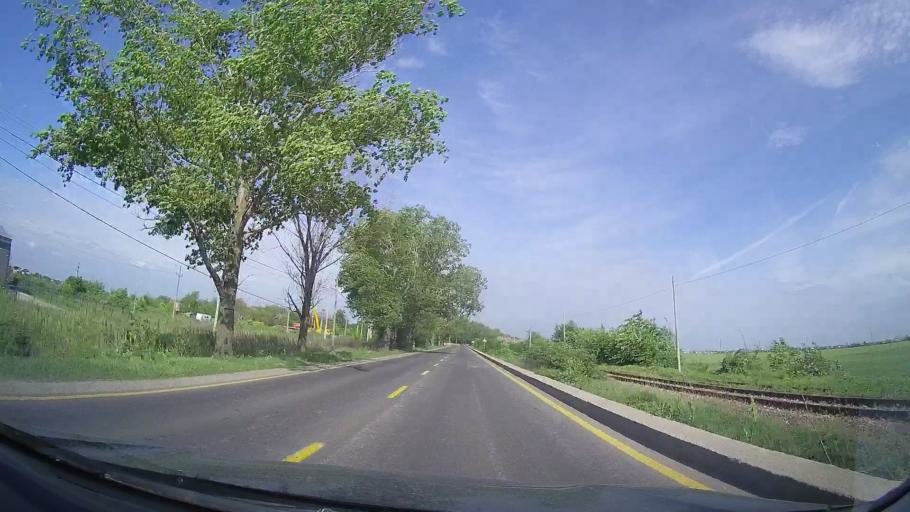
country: RO
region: Ilfov
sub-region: Comuna Magurele
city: Magurele
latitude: 44.3618
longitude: 26.0286
